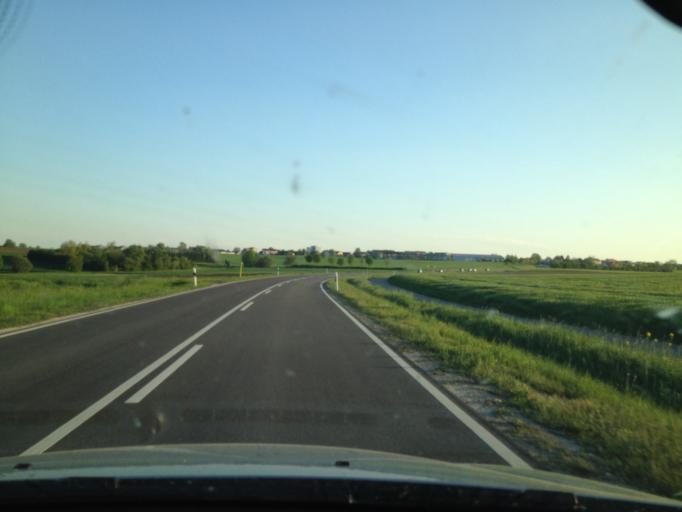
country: DE
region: Bavaria
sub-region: Regierungsbezirk Mittelfranken
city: Rothenburg ob der Tauber
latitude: 49.3942
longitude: 10.1973
